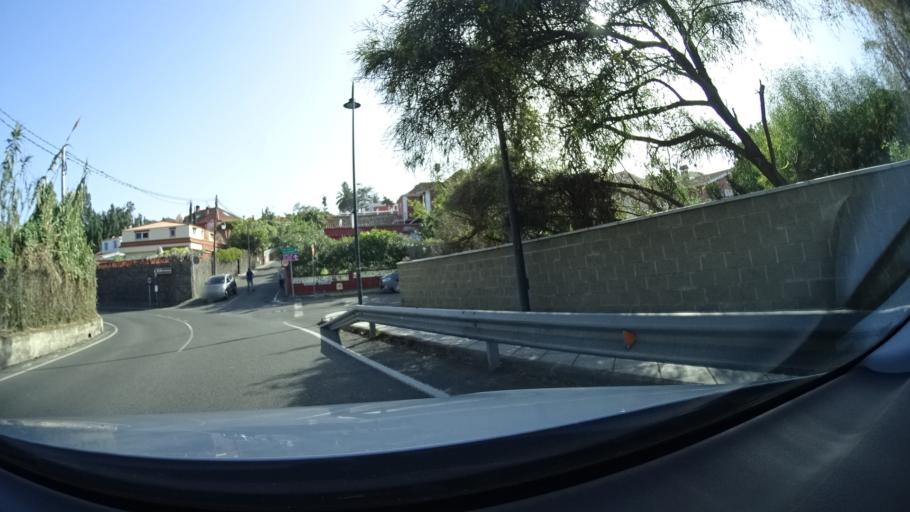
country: ES
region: Canary Islands
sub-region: Provincia de Las Palmas
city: Santa Brigida
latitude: 28.0434
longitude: -15.4771
